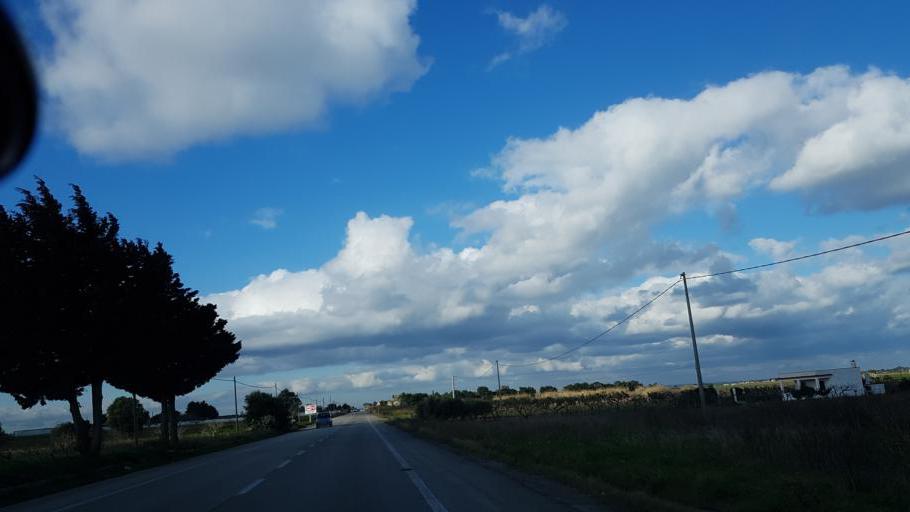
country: IT
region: Apulia
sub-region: Provincia di Brindisi
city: Brindisi
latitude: 40.6466
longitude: 17.8911
